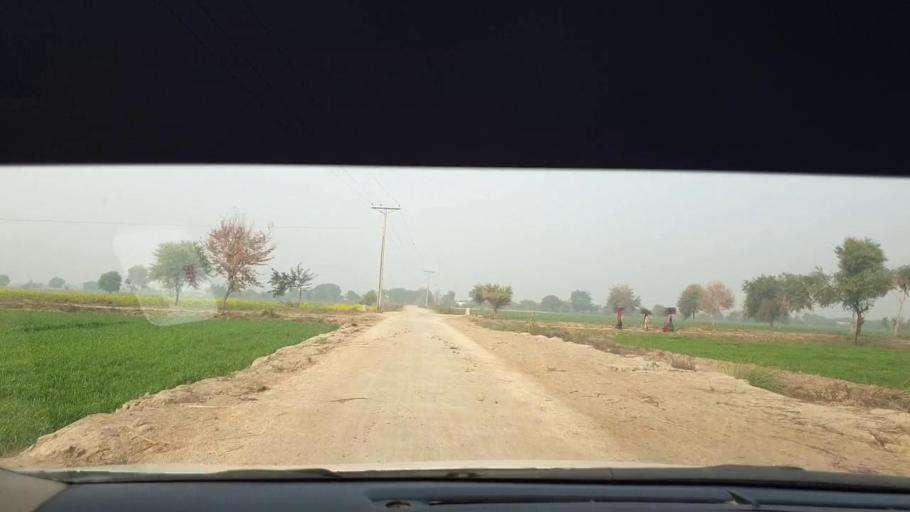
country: PK
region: Sindh
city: Berani
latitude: 25.7981
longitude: 68.8519
